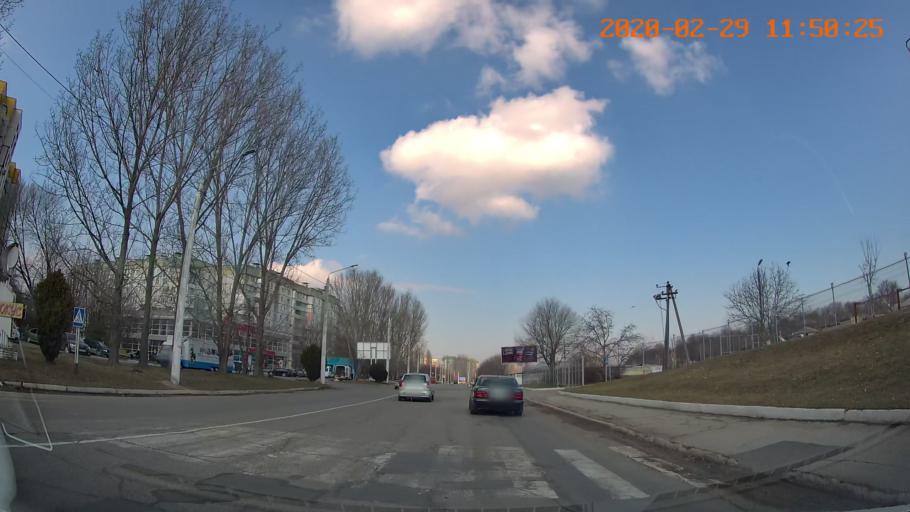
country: MD
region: Telenesti
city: Ribnita
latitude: 47.7578
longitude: 28.9908
